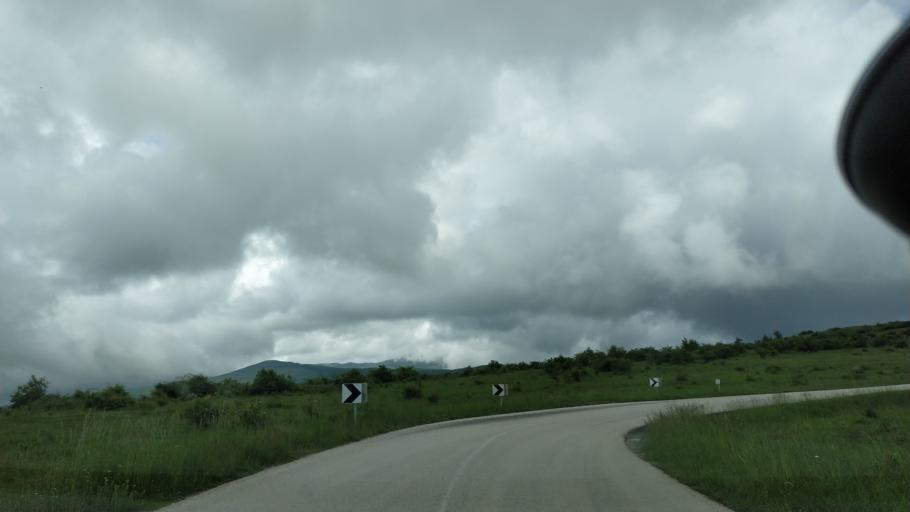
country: RS
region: Central Serbia
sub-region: Zajecarski Okrug
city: Soko Banja
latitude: 43.7061
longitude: 21.9369
